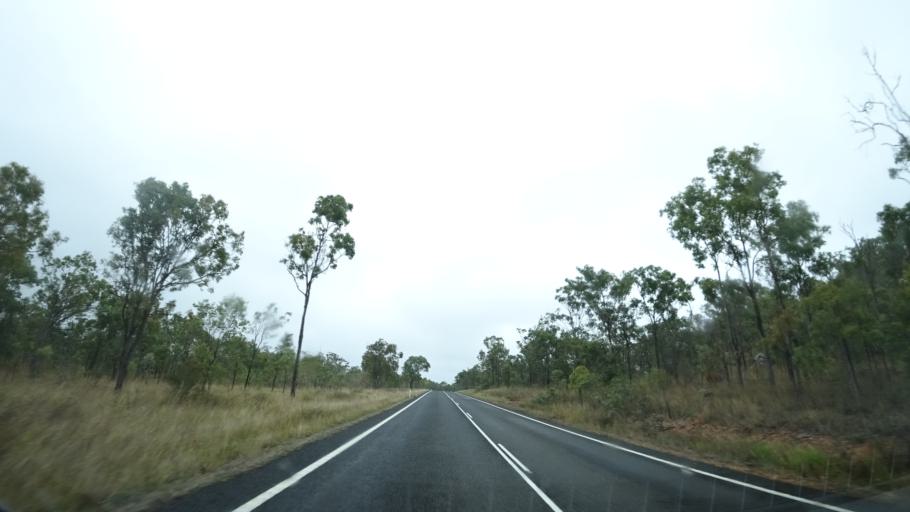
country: AU
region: Queensland
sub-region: Tablelands
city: Ravenshoe
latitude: -17.6975
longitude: 145.1840
